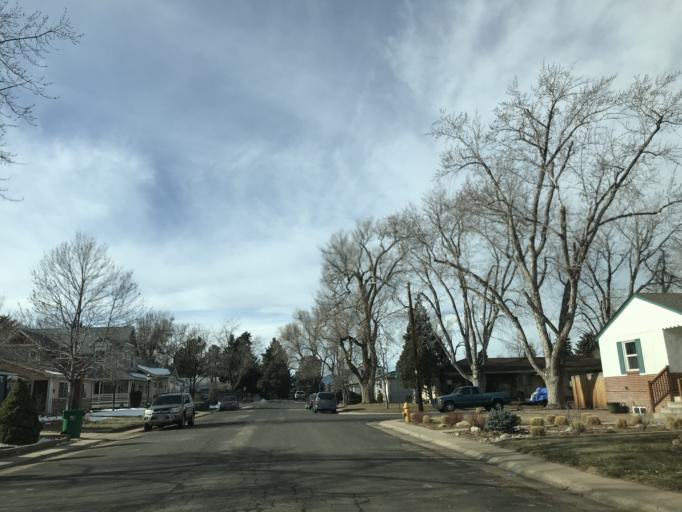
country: US
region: Colorado
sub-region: Arapahoe County
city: Littleton
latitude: 39.6052
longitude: -105.0147
